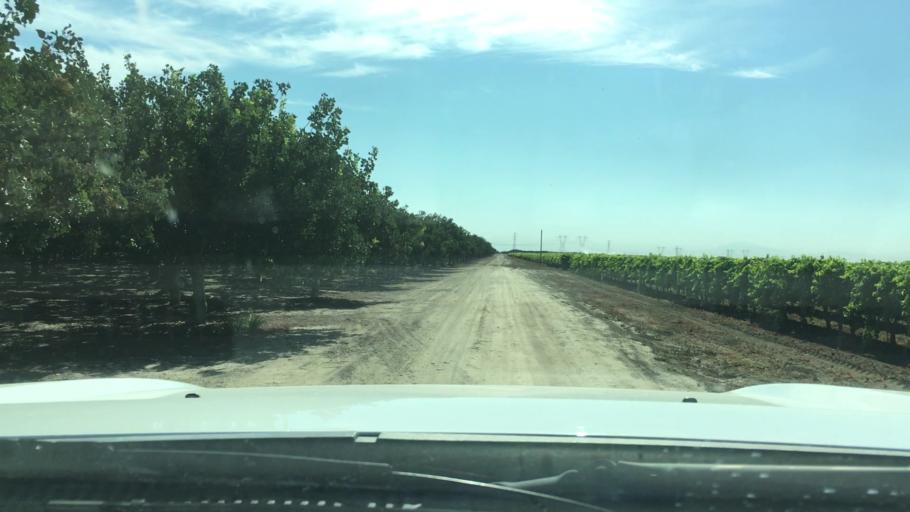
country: US
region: California
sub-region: Kern County
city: Buttonwillow
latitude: 35.3657
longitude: -119.3940
